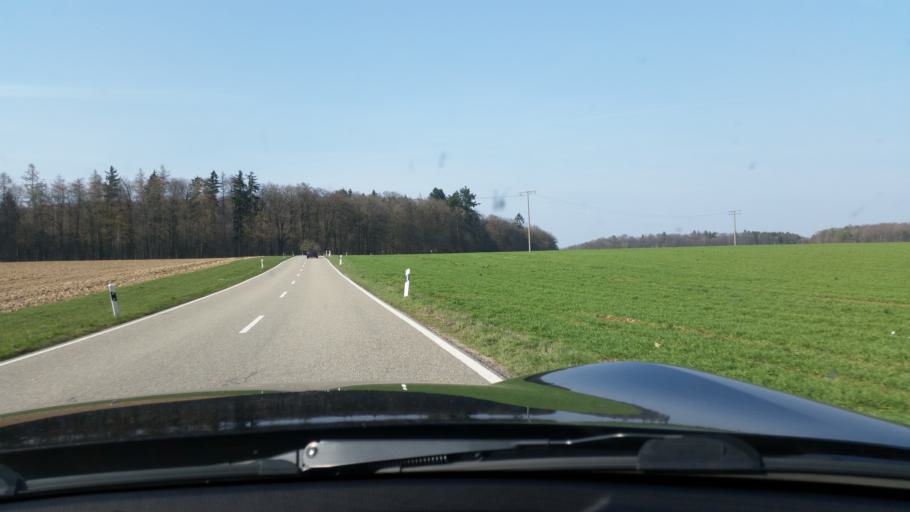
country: DE
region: Baden-Wuerttemberg
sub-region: Regierungsbezirk Stuttgart
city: Mockmuhl
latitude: 49.3260
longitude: 9.3169
